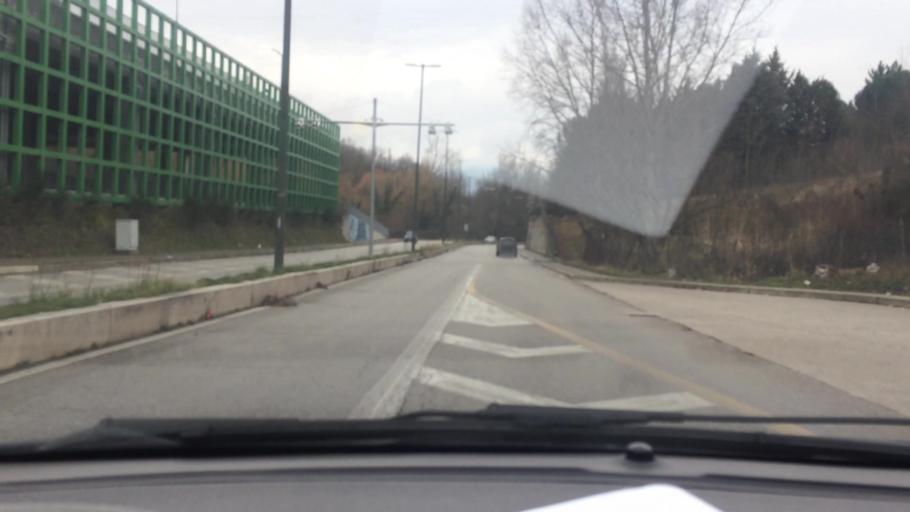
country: IT
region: Basilicate
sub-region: Provincia di Potenza
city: Potenza
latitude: 40.6366
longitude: 15.7954
